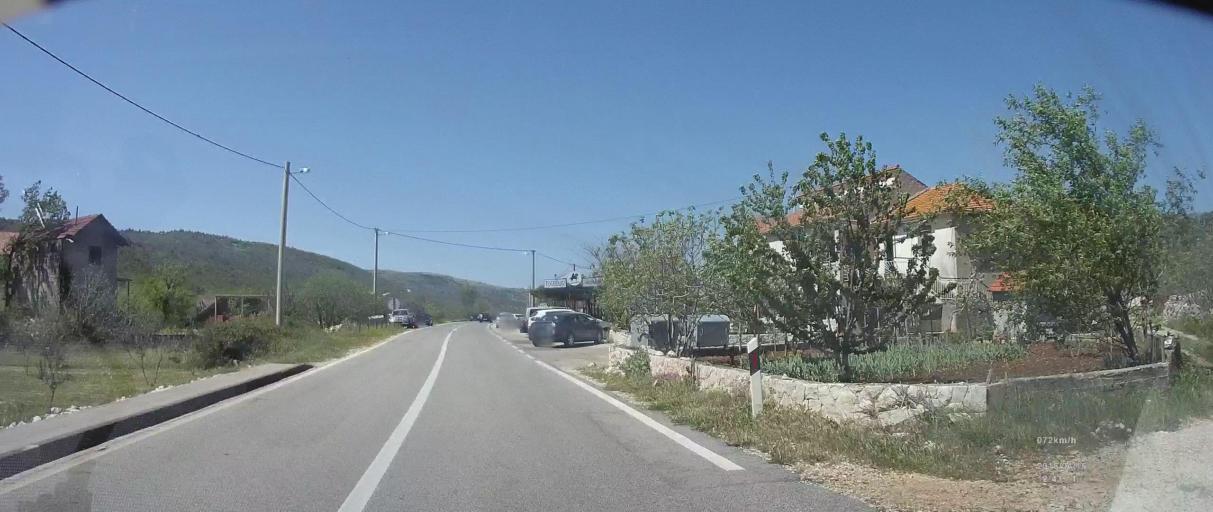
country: HR
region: Sibensko-Kniniska
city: Rogoznica
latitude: 43.6314
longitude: 16.0786
